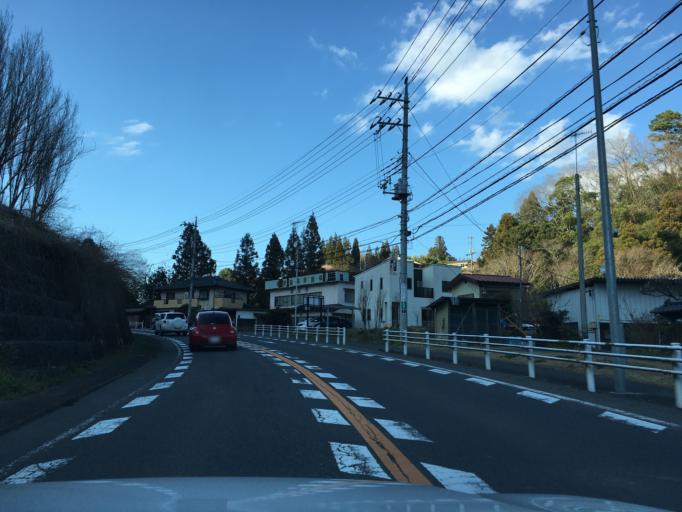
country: JP
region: Ibaraki
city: Daigo
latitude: 36.7504
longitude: 140.3843
